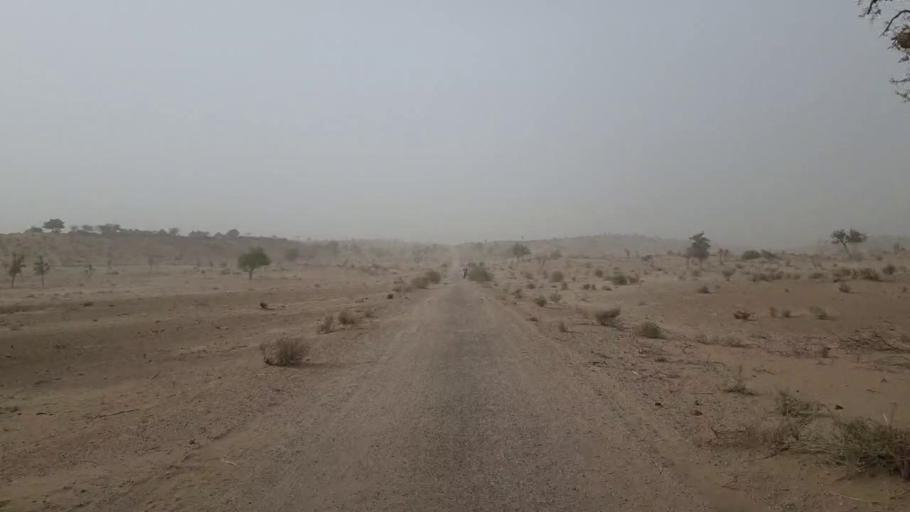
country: PK
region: Sindh
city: Islamkot
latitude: 24.5523
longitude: 70.3604
